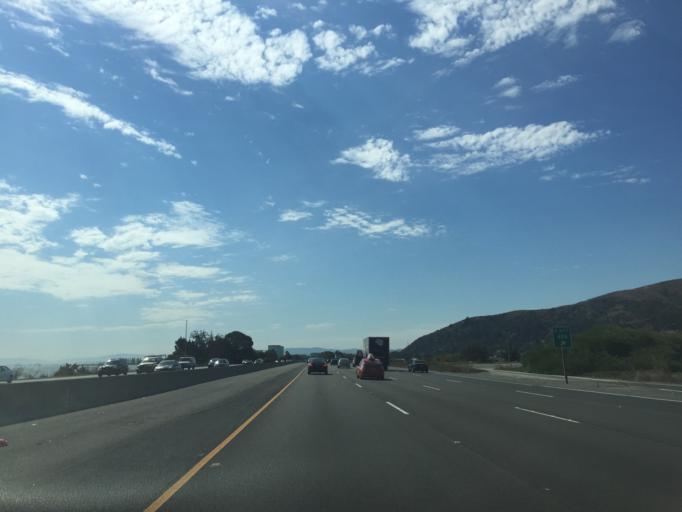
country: US
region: California
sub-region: San Mateo County
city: Brisbane
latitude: 37.6928
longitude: -122.3916
